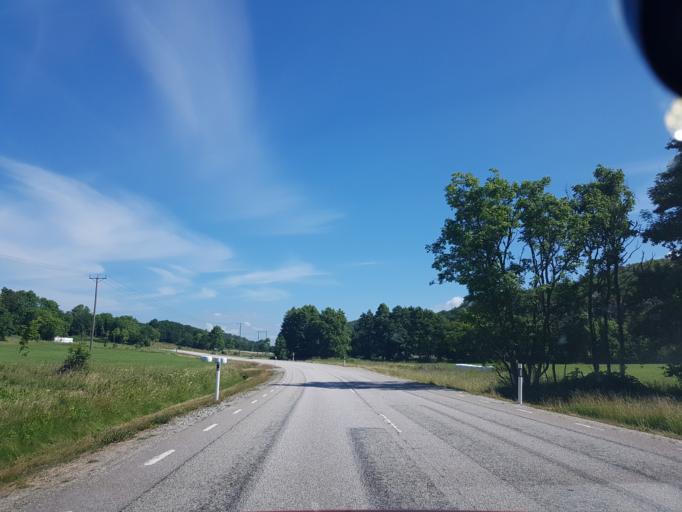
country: SE
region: Vaestra Goetaland
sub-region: Lysekils Kommun
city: Lysekil
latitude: 58.1659
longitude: 11.4811
